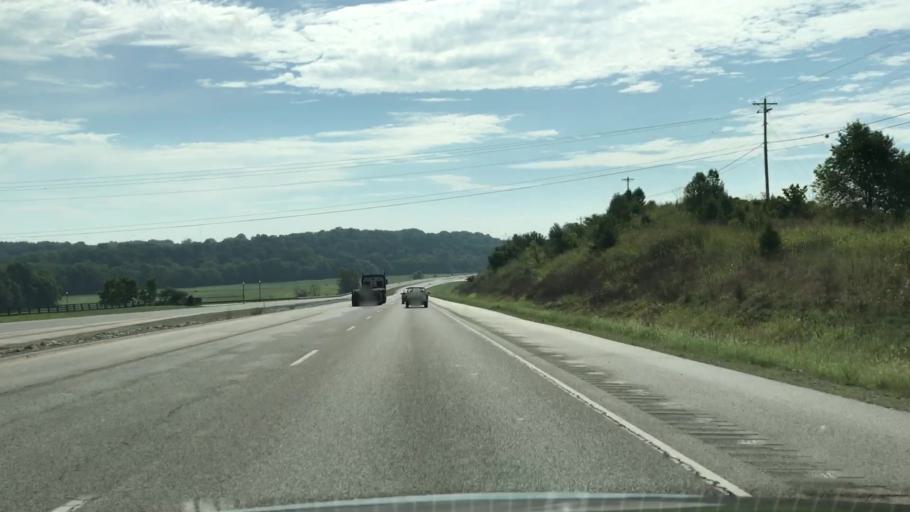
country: US
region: Kentucky
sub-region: Warren County
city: Plano
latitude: 36.9016
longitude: -86.3926
